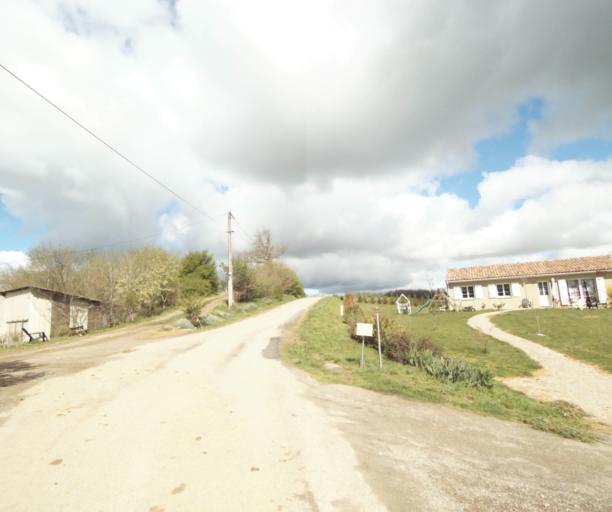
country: FR
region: Midi-Pyrenees
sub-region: Departement de l'Ariege
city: Saverdun
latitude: 43.1874
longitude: 1.5379
